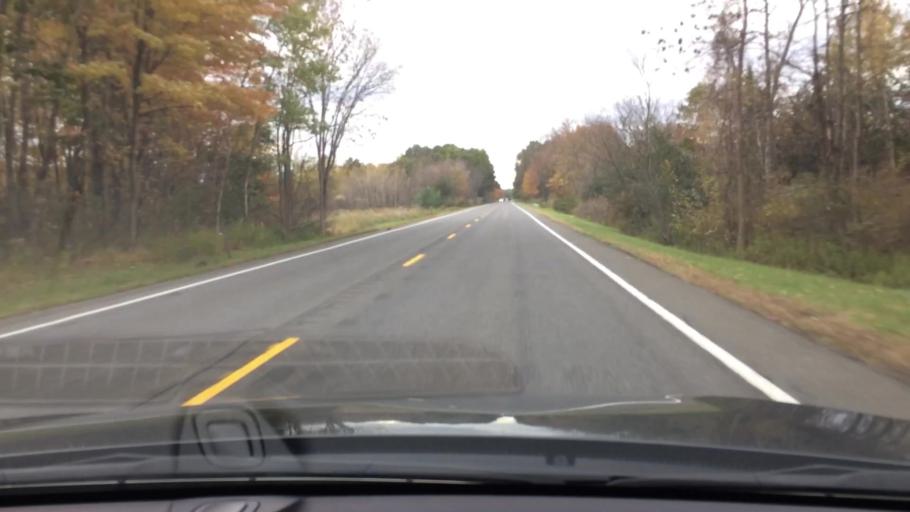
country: US
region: New York
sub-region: Columbia County
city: Kinderhook
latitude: 42.3488
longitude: -73.7050
